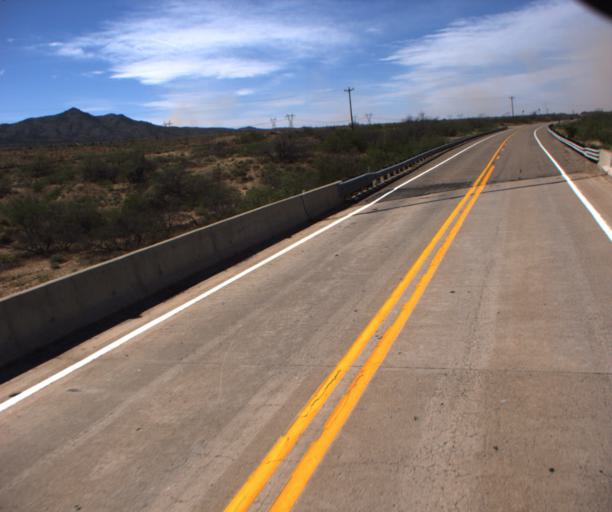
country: US
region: Arizona
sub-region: Mohave County
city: New Kingman-Butler
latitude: 35.3801
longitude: -113.7289
